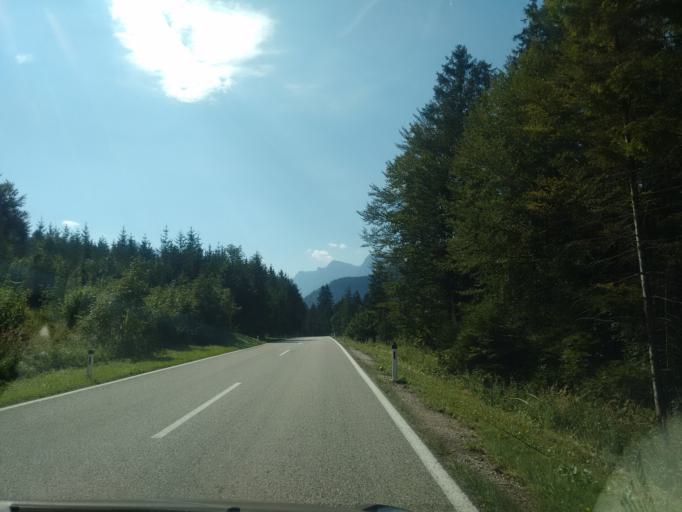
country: AT
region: Upper Austria
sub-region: Politischer Bezirk Gmunden
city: Gruenau im Almtal
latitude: 47.8005
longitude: 13.9532
